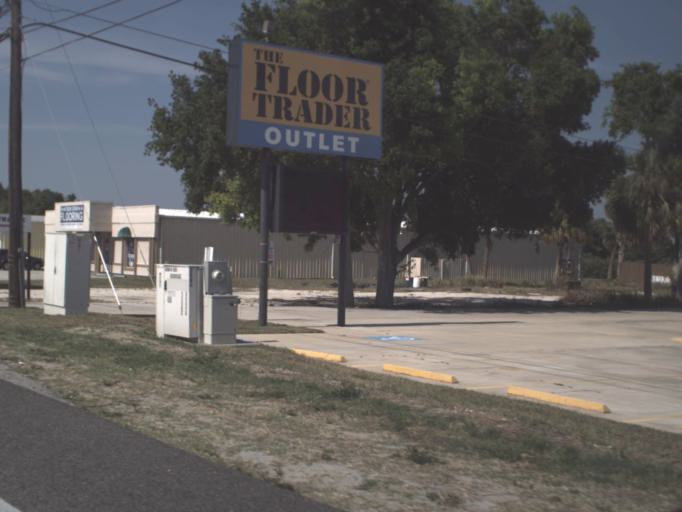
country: US
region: Florida
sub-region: Brevard County
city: Sharpes
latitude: 28.4148
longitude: -80.7550
